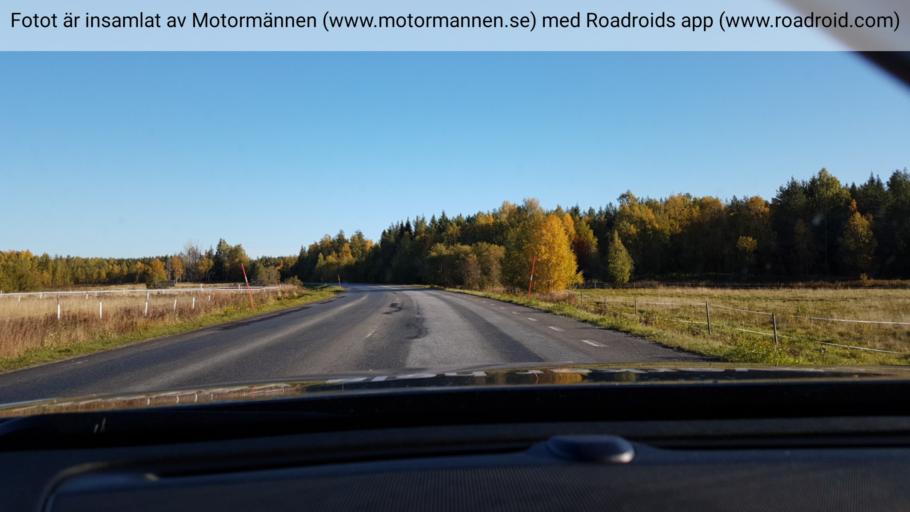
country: SE
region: Norrbotten
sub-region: Bodens Kommun
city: Boden
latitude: 65.8364
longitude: 21.7251
